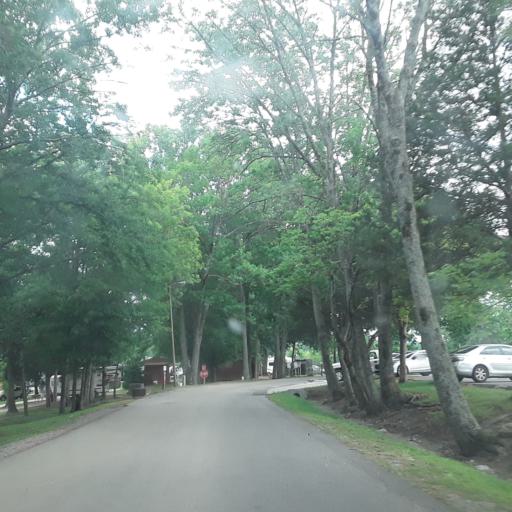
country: US
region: Tennessee
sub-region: Wilson County
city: Green Hill
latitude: 36.1576
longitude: -86.6039
